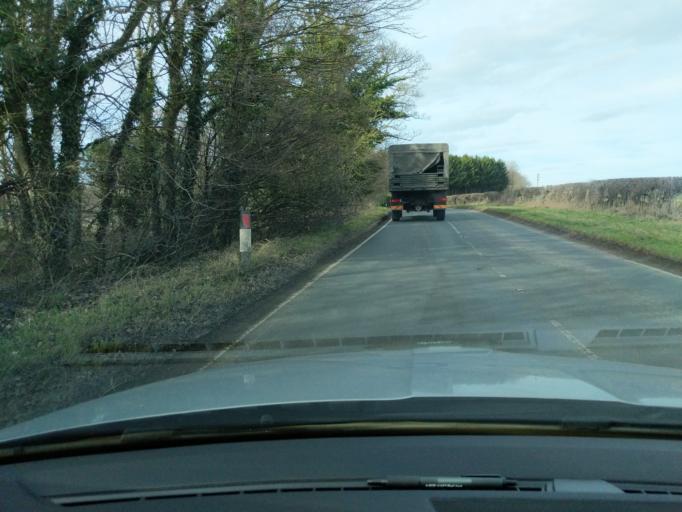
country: GB
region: England
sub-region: North Yorkshire
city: Catterick Garrison
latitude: 54.3962
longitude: -1.6880
